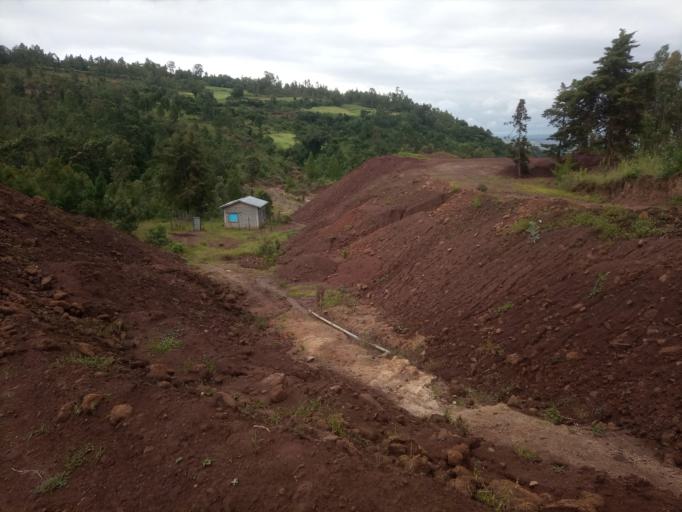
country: ET
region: Southern Nations, Nationalities, and People's Region
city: K'olito
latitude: 7.3769
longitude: 37.8859
